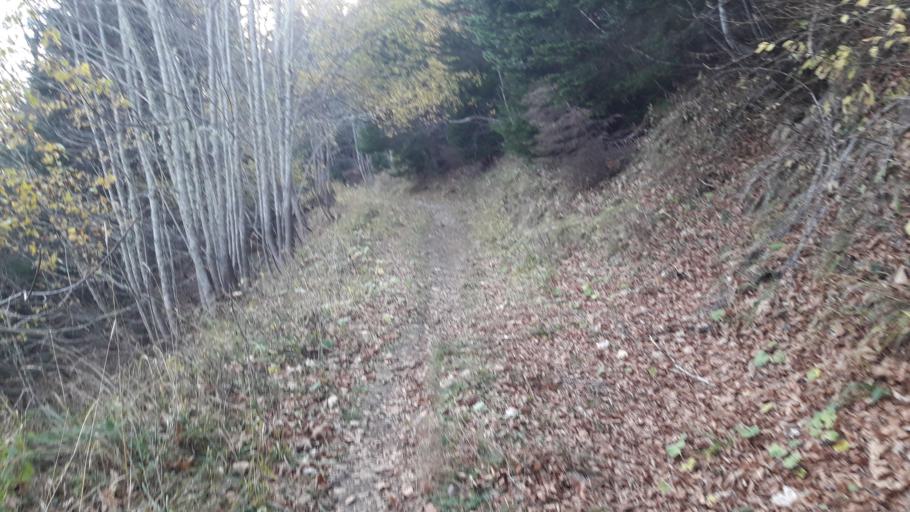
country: FR
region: Rhone-Alpes
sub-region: Departement de l'Isere
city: Bernin
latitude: 45.2969
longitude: 5.8348
